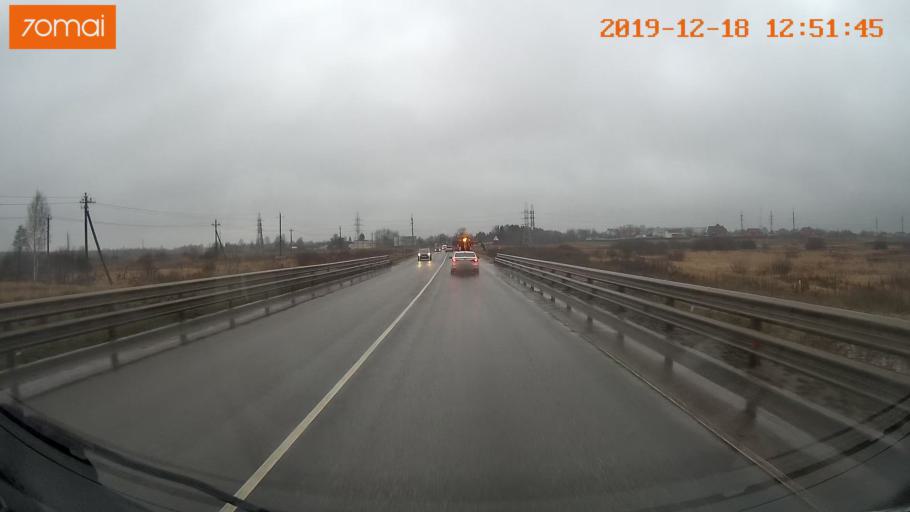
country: RU
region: Moskovskaya
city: Klin
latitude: 56.3061
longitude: 36.6851
